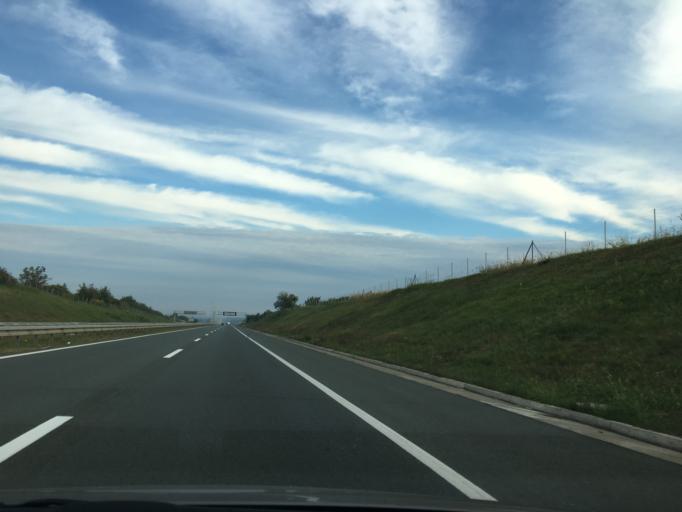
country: RS
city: Beska
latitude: 45.1600
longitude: 20.0814
